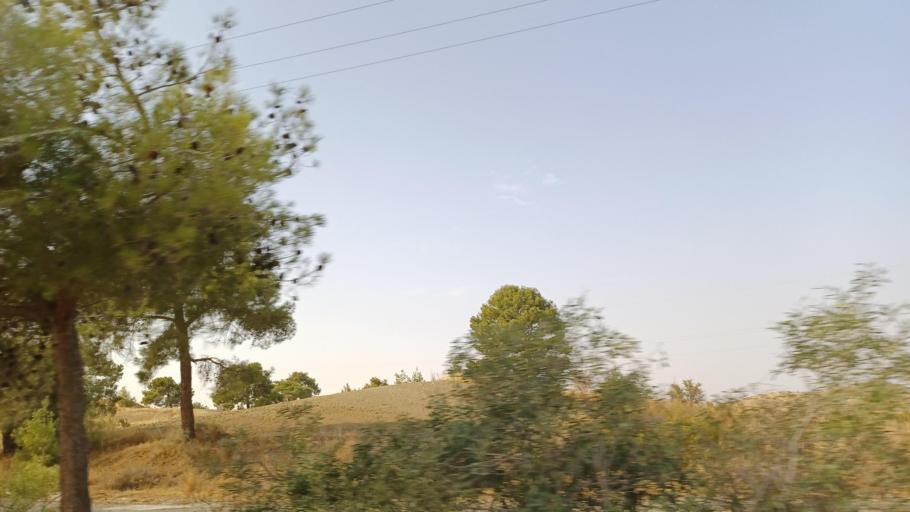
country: CY
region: Lefkosia
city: Kakopetria
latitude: 35.0756
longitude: 32.9453
